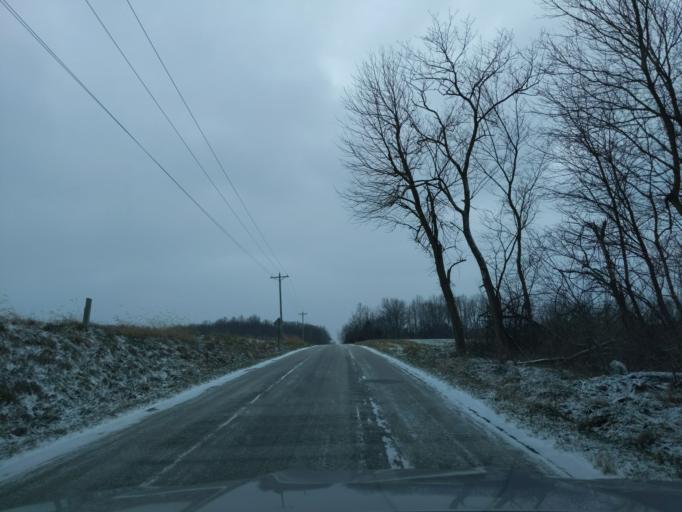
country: US
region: Indiana
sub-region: Decatur County
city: Greensburg
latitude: 39.2442
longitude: -85.4685
